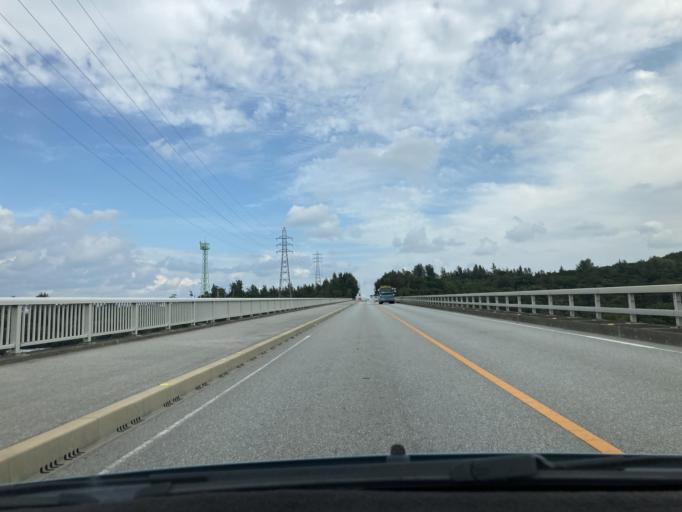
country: JP
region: Okinawa
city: Ishikawa
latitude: 26.4947
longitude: 127.8574
